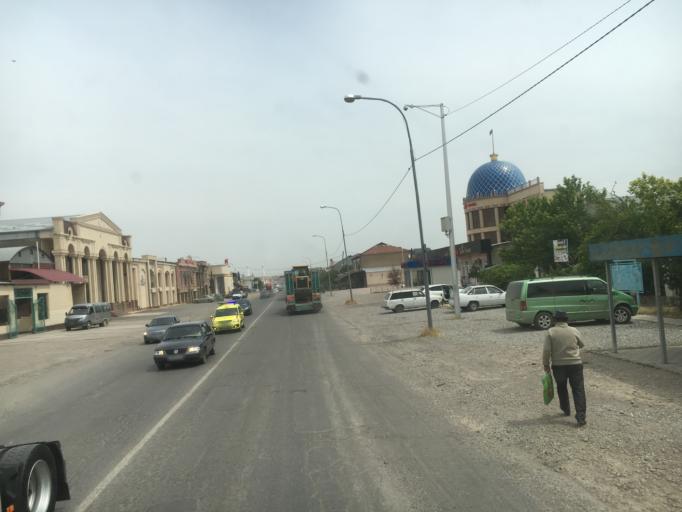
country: KZ
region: Ongtustik Qazaqstan
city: Shymkent
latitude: 42.3448
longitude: 69.5253
